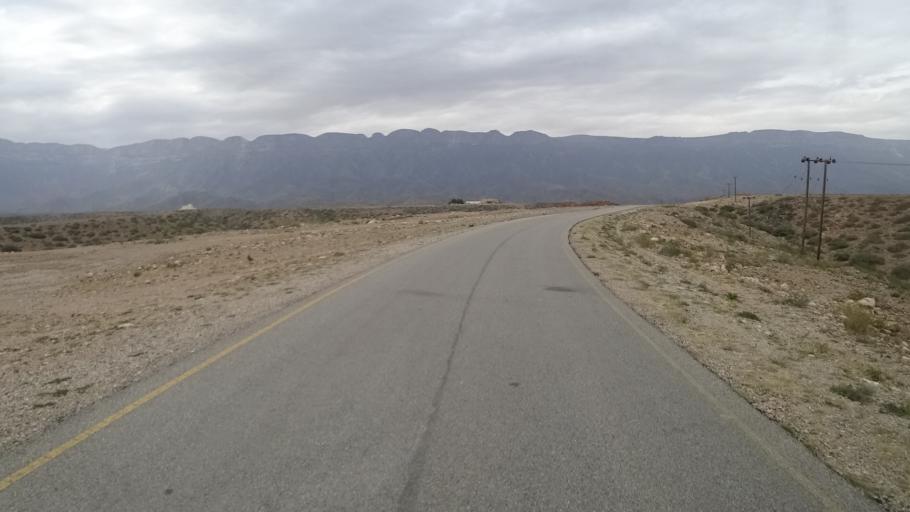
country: OM
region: Zufar
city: Salalah
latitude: 17.1475
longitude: 55.0050
